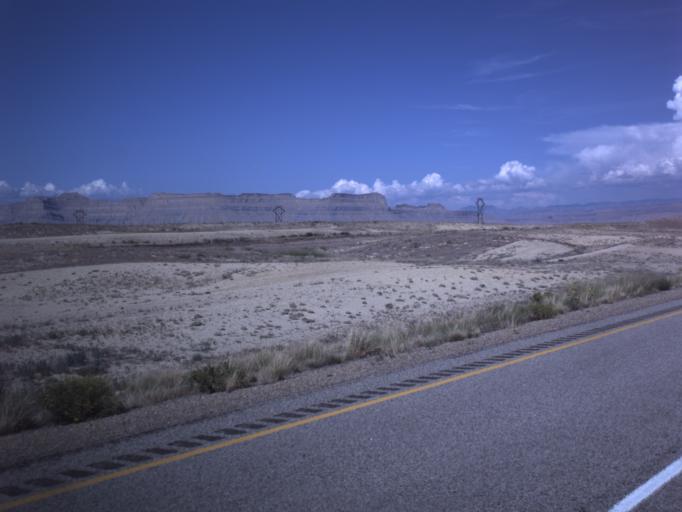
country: US
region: Utah
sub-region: Carbon County
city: East Carbon City
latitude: 38.9640
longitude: -110.2799
